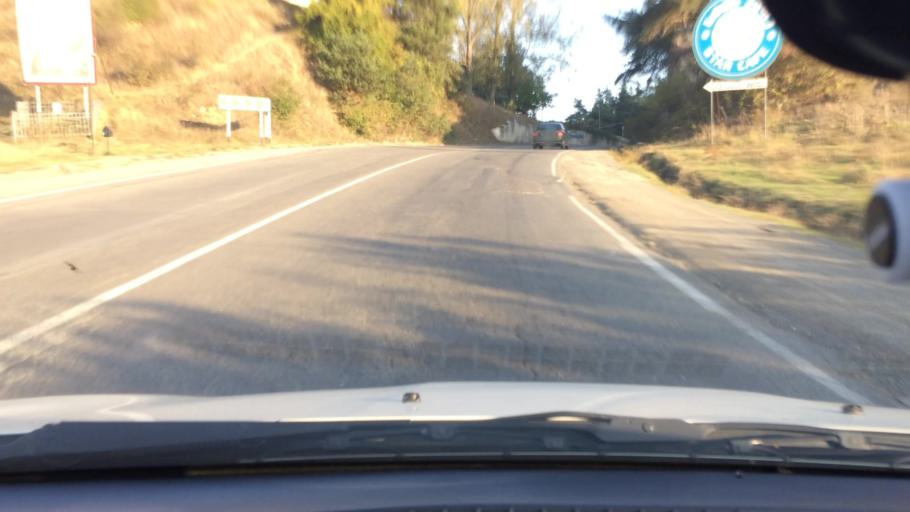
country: GE
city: Surami
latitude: 42.0200
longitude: 43.5658
